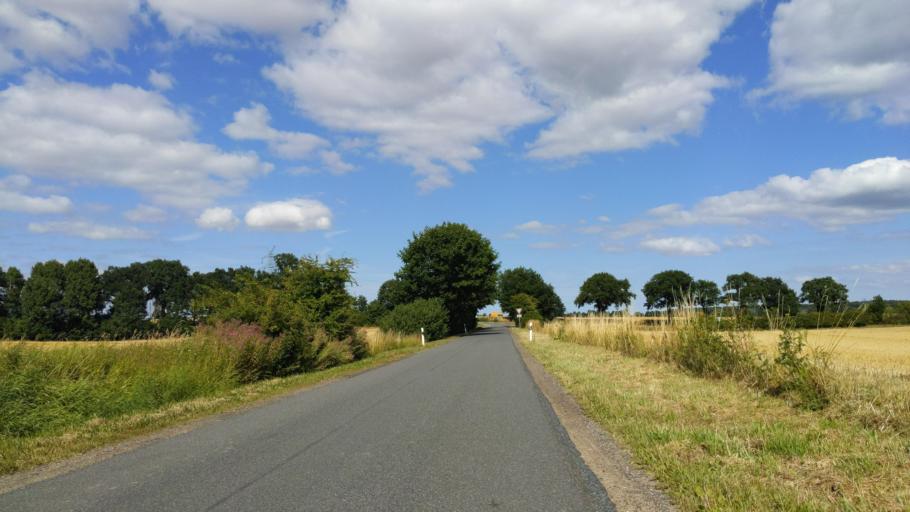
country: DE
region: Schleswig-Holstein
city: Stockelsdorf
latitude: 53.9171
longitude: 10.6204
